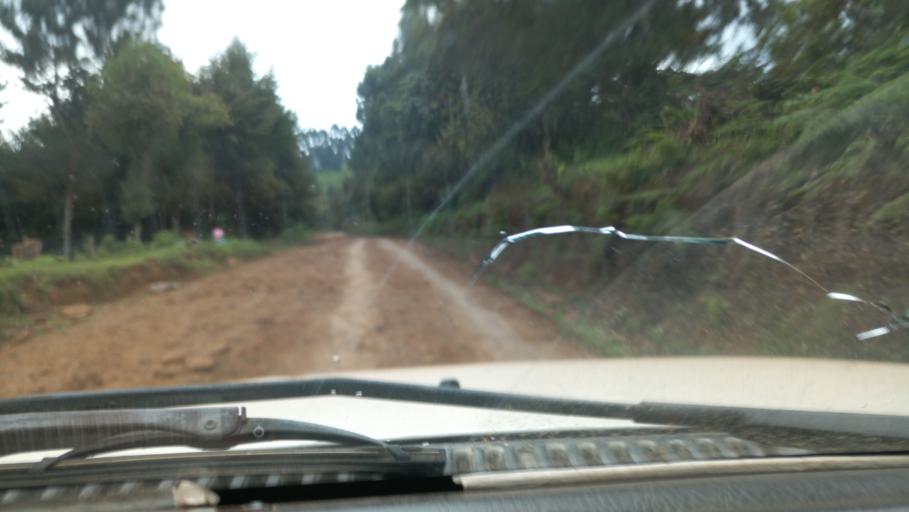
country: KE
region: Nyeri
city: Othaya
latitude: -0.6079
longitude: 36.8479
